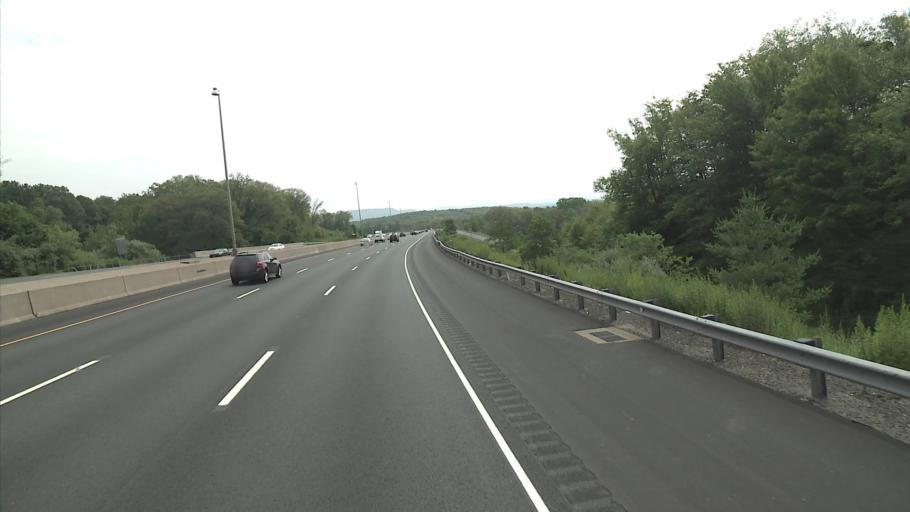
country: US
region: Connecticut
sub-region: New Haven County
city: Prospect
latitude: 41.5412
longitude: -72.9532
